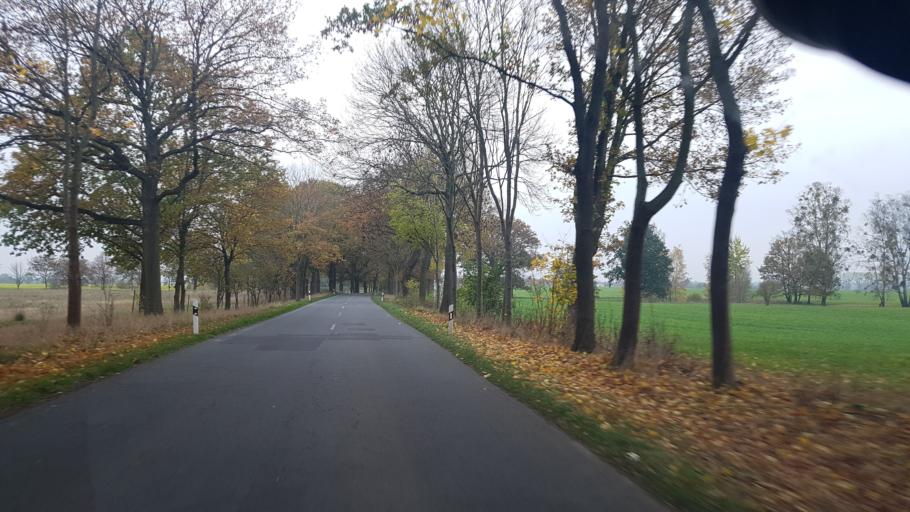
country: DE
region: Brandenburg
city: Schonermark
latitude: 52.9217
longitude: 13.1209
